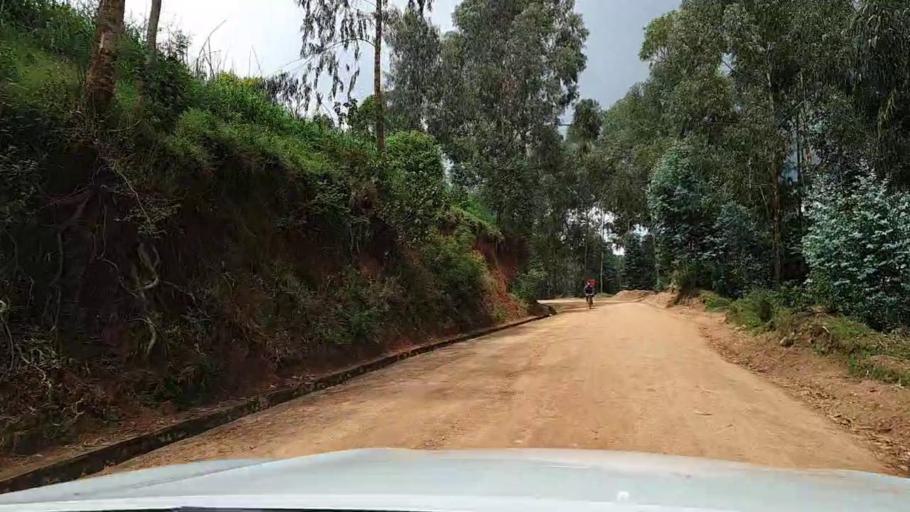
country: RW
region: Southern Province
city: Nzega
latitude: -2.4283
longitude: 29.4419
